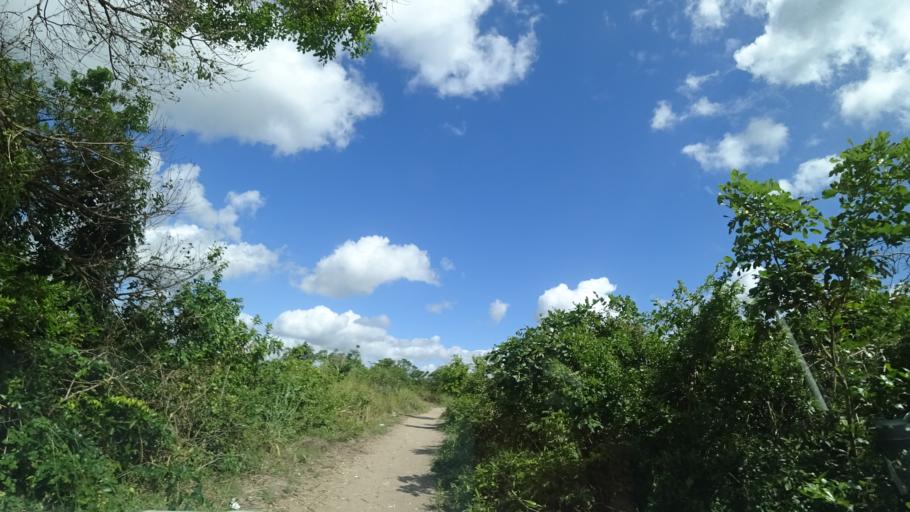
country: MZ
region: Sofala
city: Dondo
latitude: -19.3598
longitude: 34.5763
